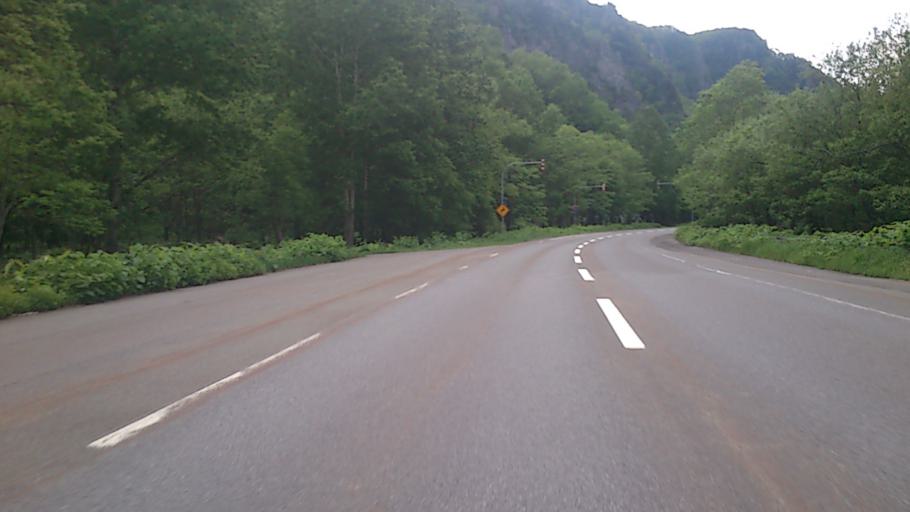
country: JP
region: Hokkaido
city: Kamikawa
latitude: 43.7532
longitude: 142.9299
